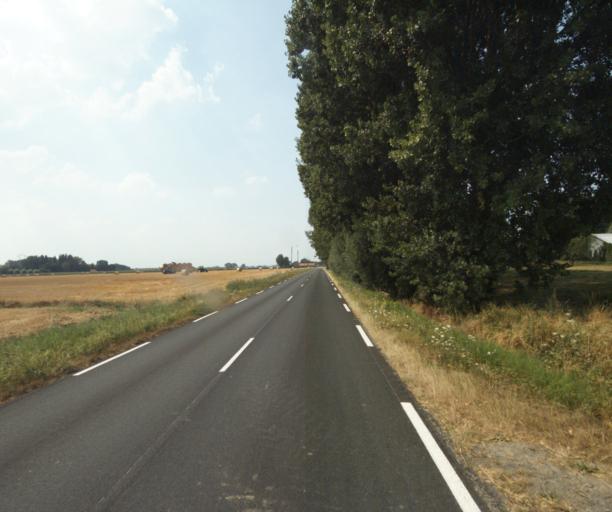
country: FR
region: Nord-Pas-de-Calais
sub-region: Departement du Nord
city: Quesnoy-sur-Deule
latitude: 50.7240
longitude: 2.9804
